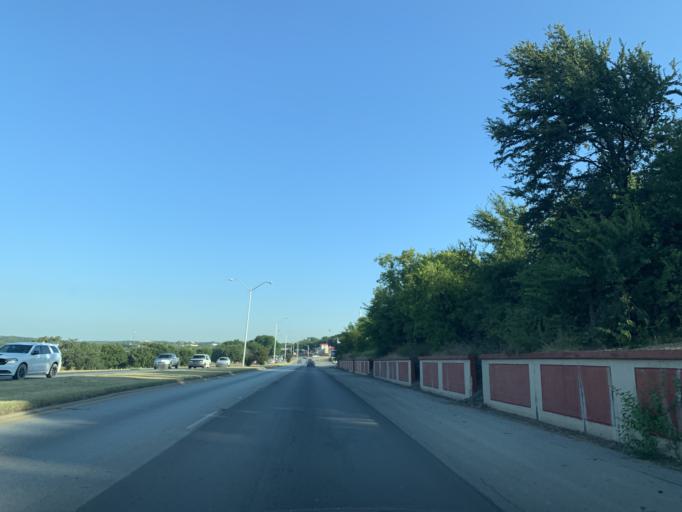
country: US
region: Texas
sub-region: Tarrant County
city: River Oaks
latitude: 32.7769
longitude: -97.3682
